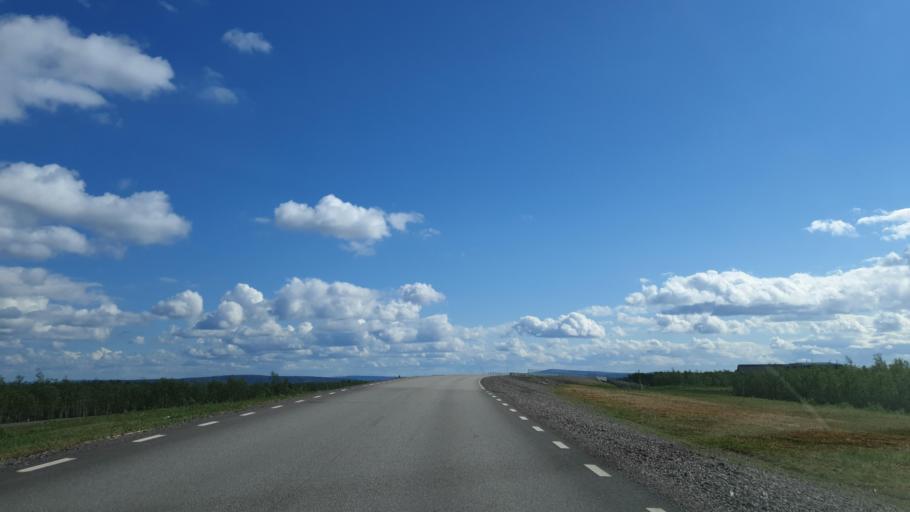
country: SE
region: Norrbotten
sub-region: Kiruna Kommun
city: Kiruna
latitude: 67.7977
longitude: 20.2341
